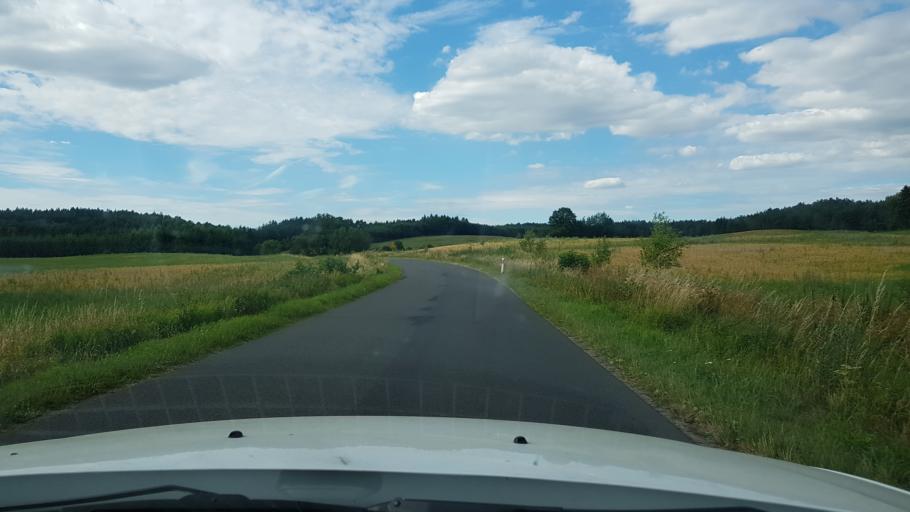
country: PL
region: West Pomeranian Voivodeship
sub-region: Powiat drawski
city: Zlocieniec
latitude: 53.4841
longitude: 16.0446
